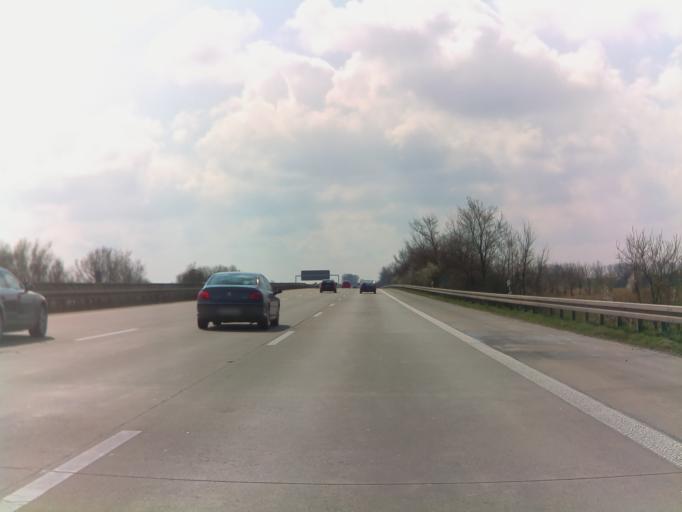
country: DE
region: Saxony-Anhalt
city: Osterfeld
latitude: 51.0877
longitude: 11.9551
